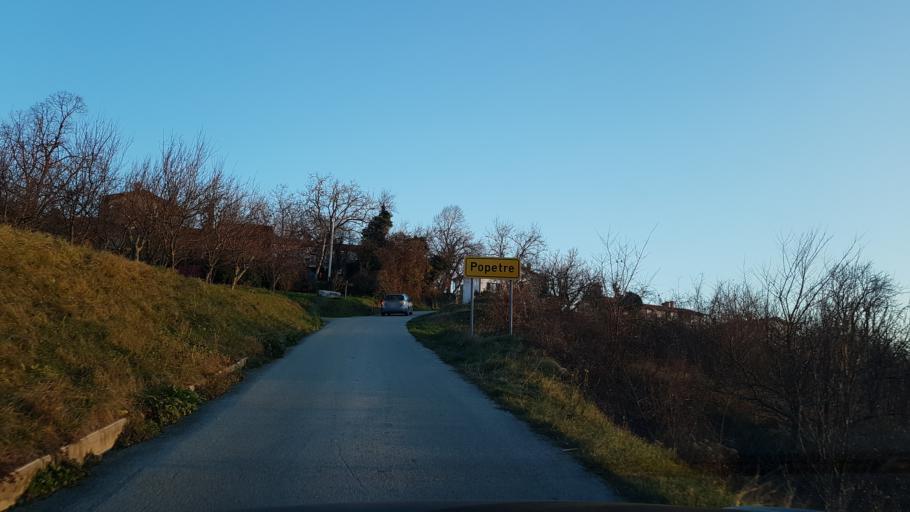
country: SI
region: Koper-Capodistria
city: Sv. Anton
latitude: 45.4989
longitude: 13.8538
